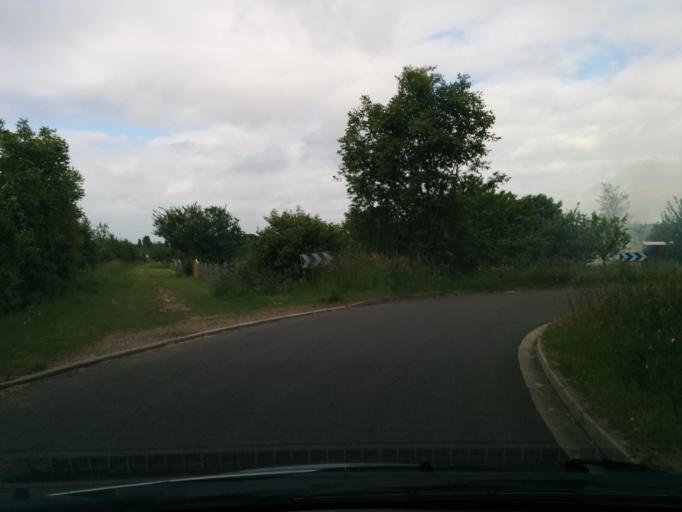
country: FR
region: Ile-de-France
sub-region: Departement des Yvelines
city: Rosny-sur-Seine
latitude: 49.0364
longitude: 1.6535
